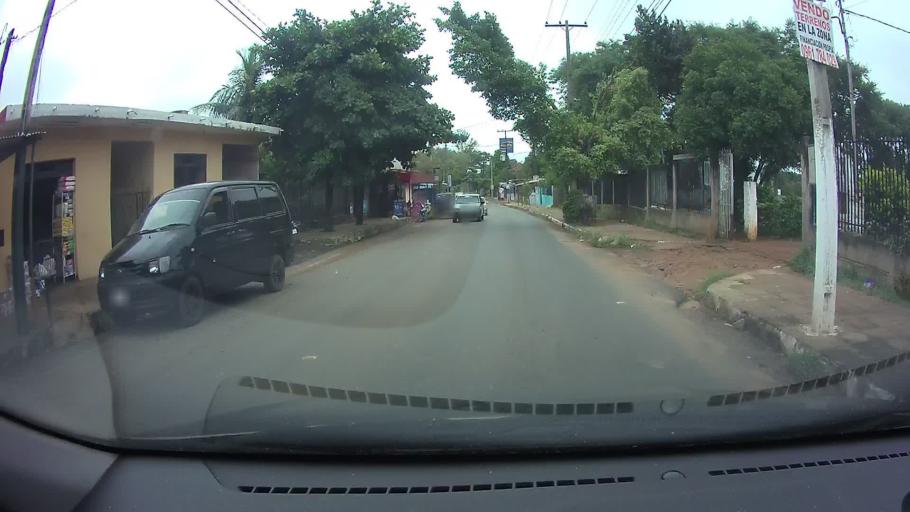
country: PY
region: Central
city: San Lorenzo
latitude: -25.3160
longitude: -57.4942
